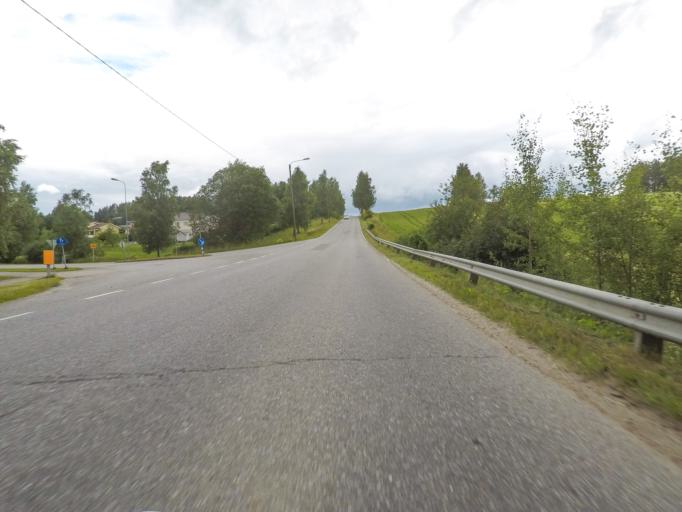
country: FI
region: Varsinais-Suomi
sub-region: Salo
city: Muurla
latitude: 60.3549
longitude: 23.2873
